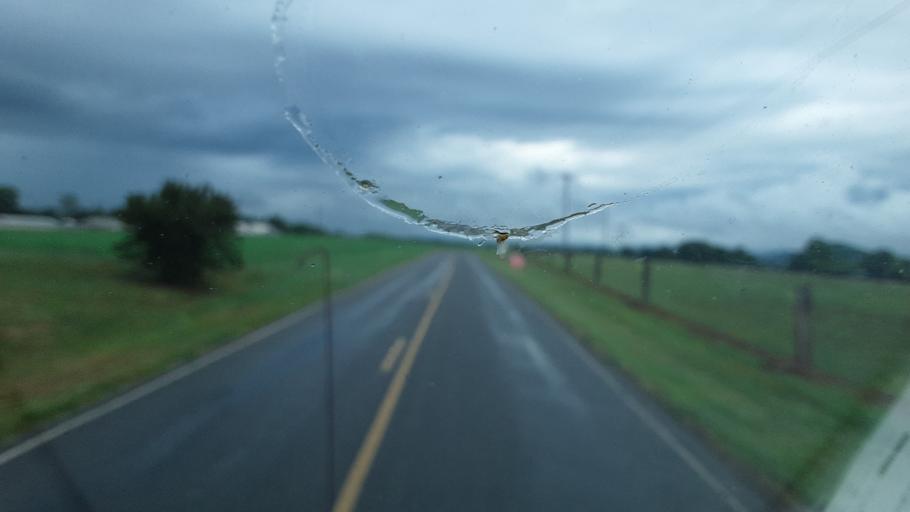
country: US
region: North Carolina
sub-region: Yadkin County
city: Jonesville
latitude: 36.0837
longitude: -80.8699
